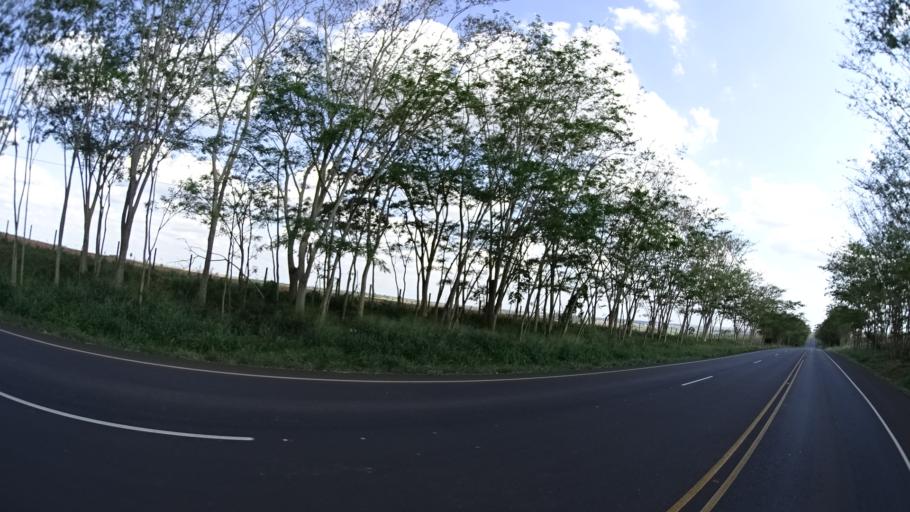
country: BR
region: Sao Paulo
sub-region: Urupes
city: Urupes
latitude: -21.0369
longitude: -49.2411
